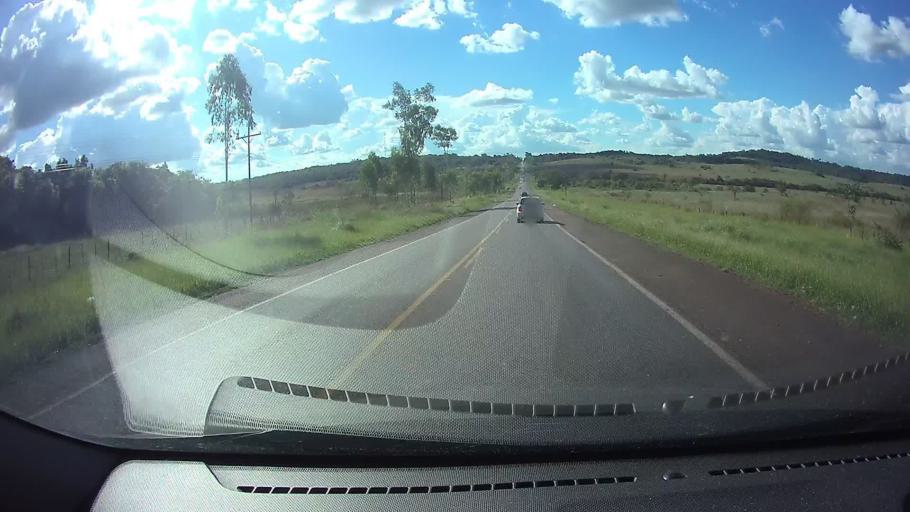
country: PY
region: Cordillera
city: Eusebio Ayala
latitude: -25.4300
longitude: -56.9149
